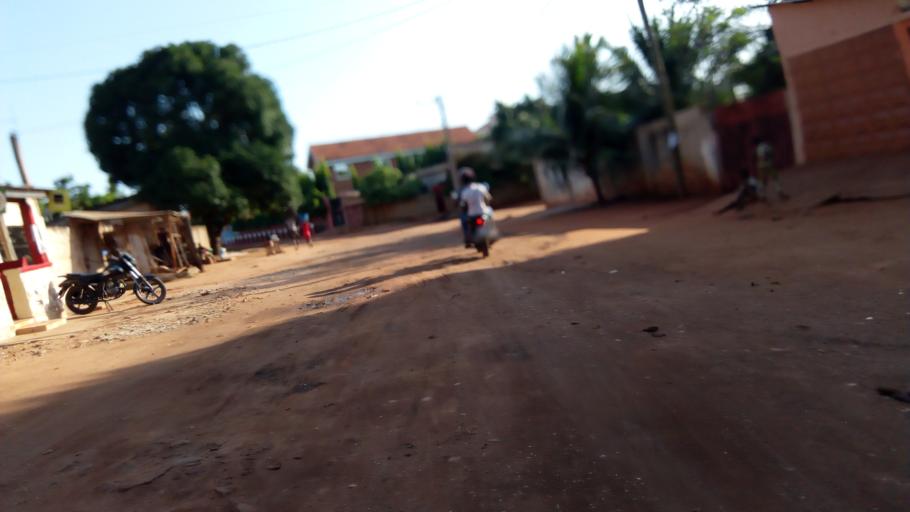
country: TG
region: Maritime
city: Lome
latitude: 6.2304
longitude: 1.1924
